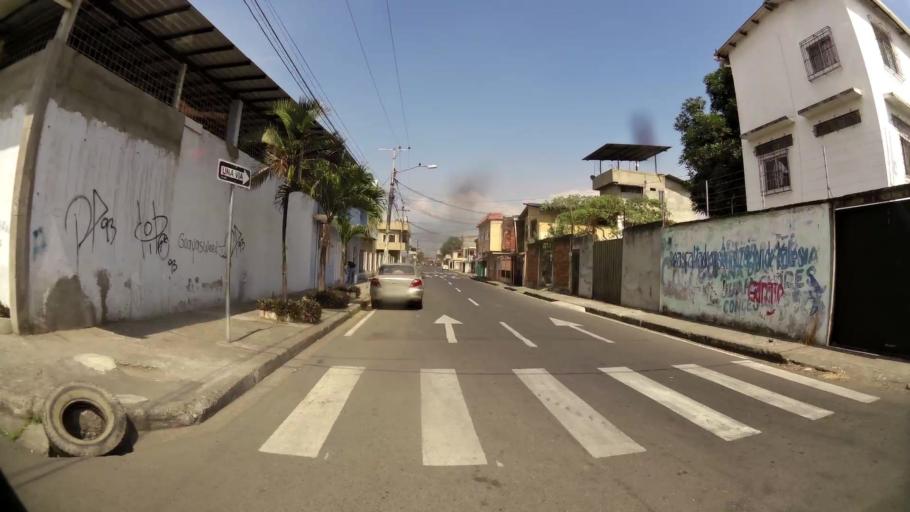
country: EC
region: Guayas
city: Eloy Alfaro
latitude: -2.1619
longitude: -79.8433
